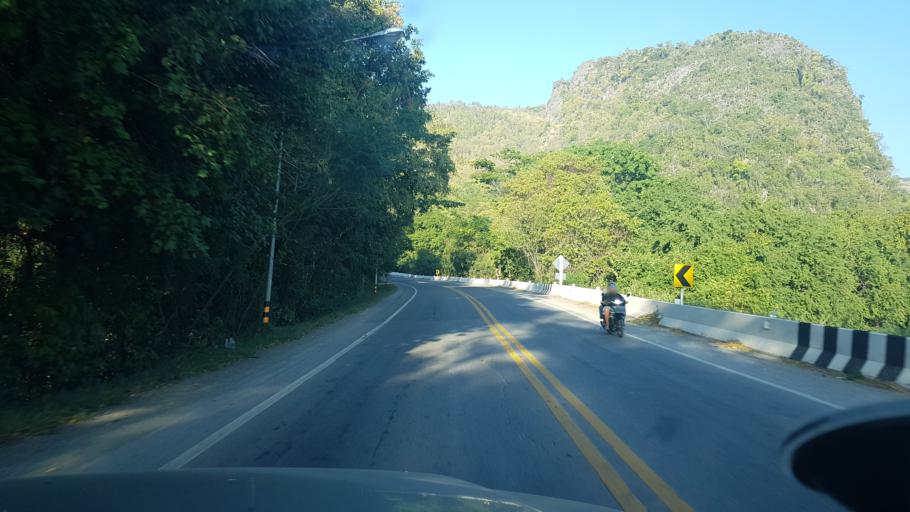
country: TH
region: Khon Kaen
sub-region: Amphoe Phu Pha Man
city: Phu Pha Man
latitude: 16.6511
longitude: 101.8045
